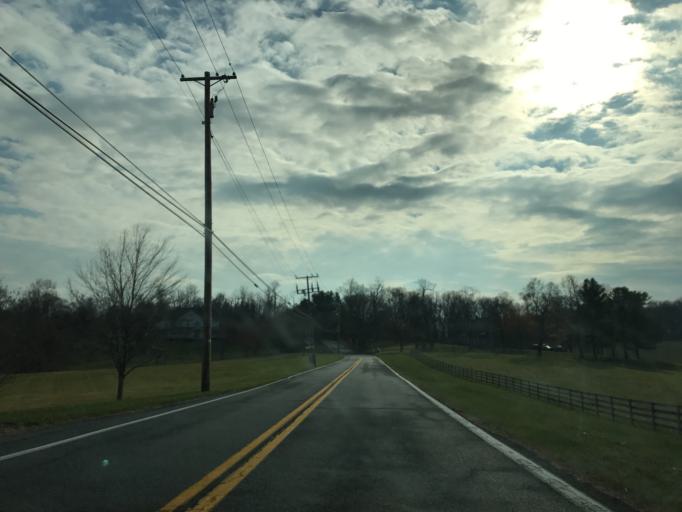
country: US
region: Maryland
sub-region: Baltimore County
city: Hunt Valley
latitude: 39.5743
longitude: -76.6020
